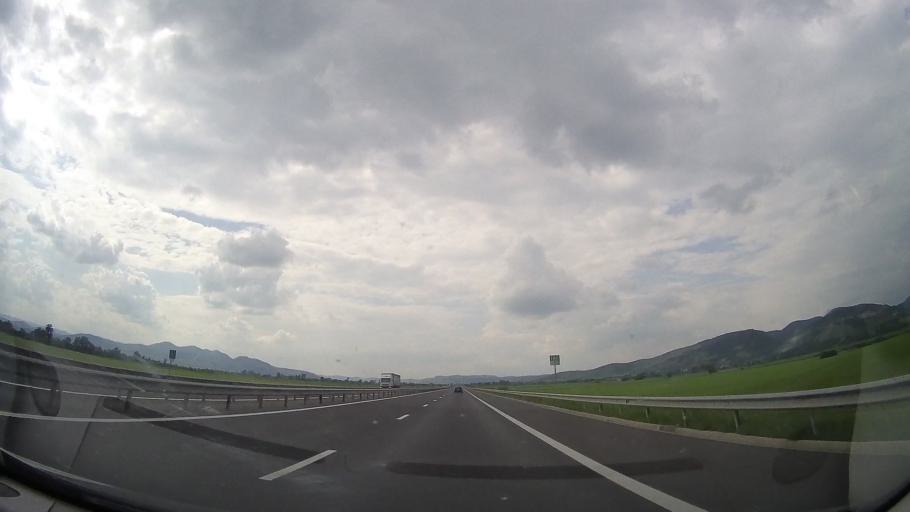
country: RO
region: Hunedoara
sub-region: Oras Simeria
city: Simeria
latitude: 45.8754
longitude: 23.0059
